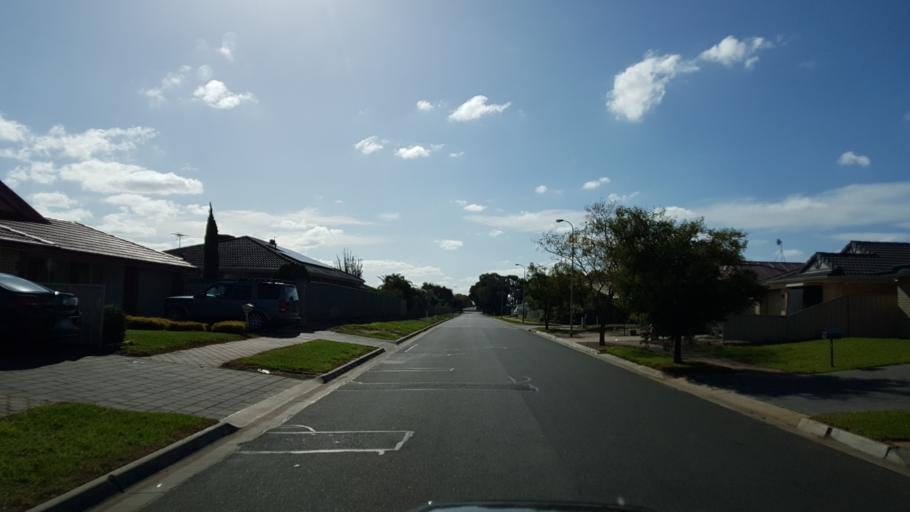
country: AU
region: South Australia
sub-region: Salisbury
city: Salisbury
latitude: -34.7658
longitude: 138.5989
